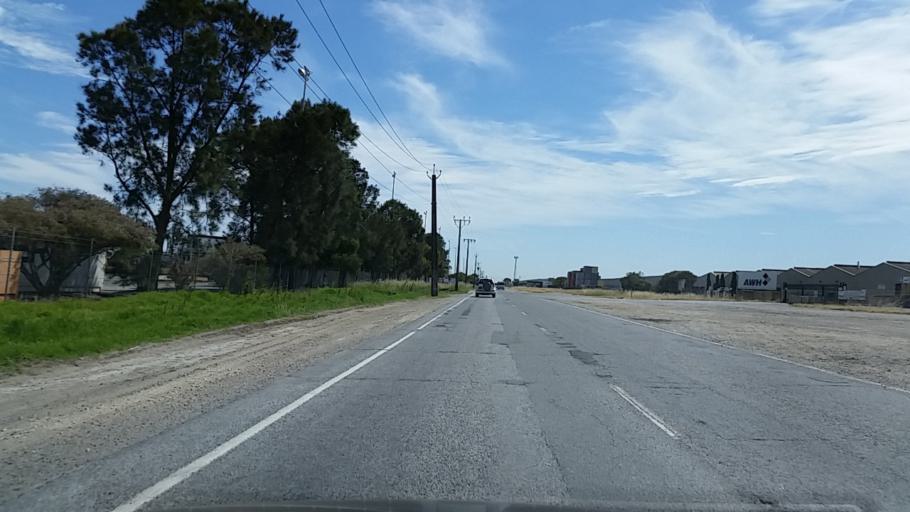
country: AU
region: South Australia
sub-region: Port Adelaide Enfield
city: Birkenhead
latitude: -34.8332
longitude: 138.5162
